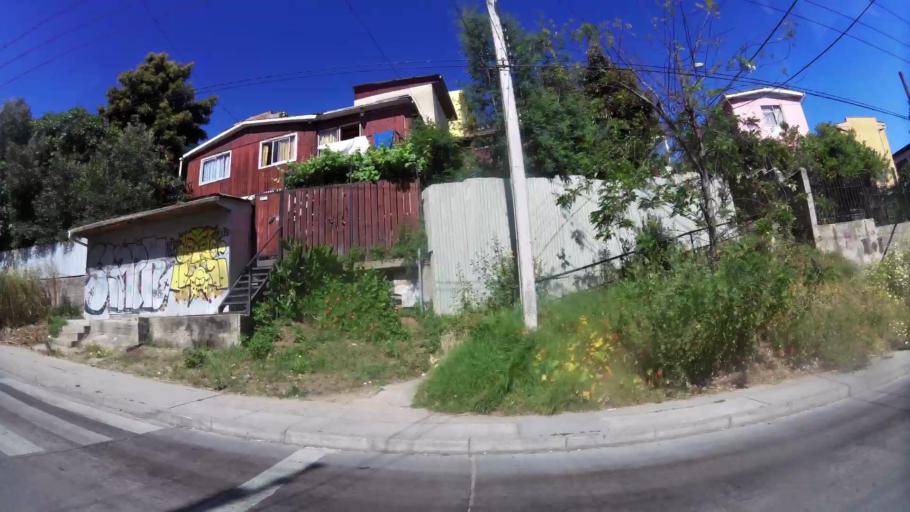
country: CL
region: Valparaiso
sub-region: Provincia de Valparaiso
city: Valparaiso
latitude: -33.0545
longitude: -71.5862
